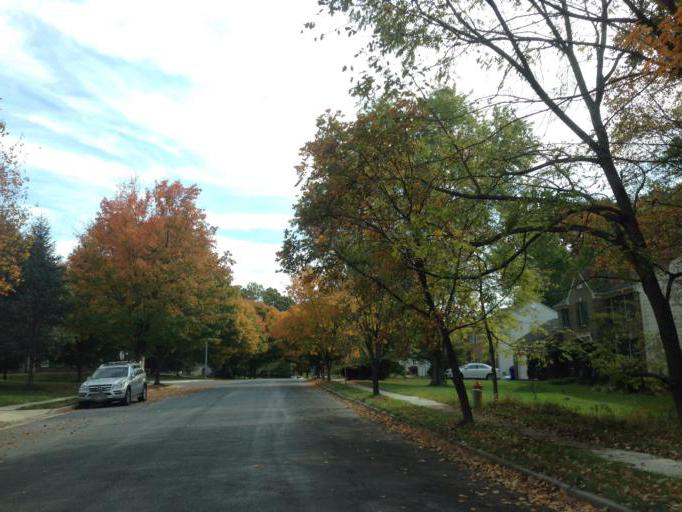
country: US
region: Maryland
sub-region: Howard County
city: Columbia
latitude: 39.2895
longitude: -76.8456
